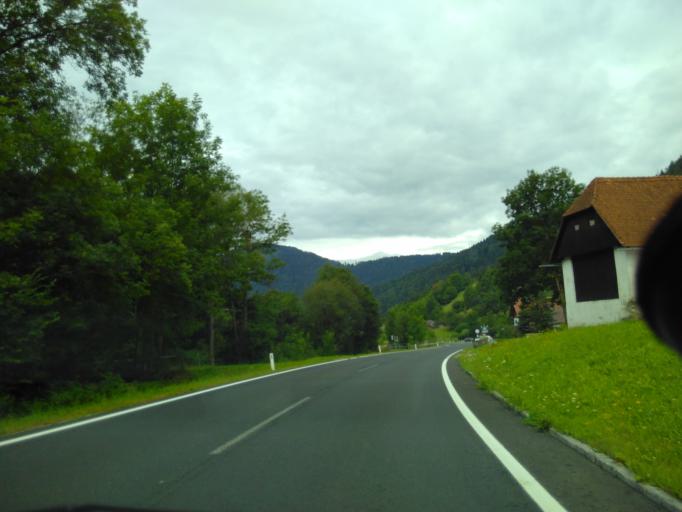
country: AT
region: Styria
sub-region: Politischer Bezirk Graz-Umgebung
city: Schrems bei Frohnleiten
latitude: 47.2747
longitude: 15.3844
